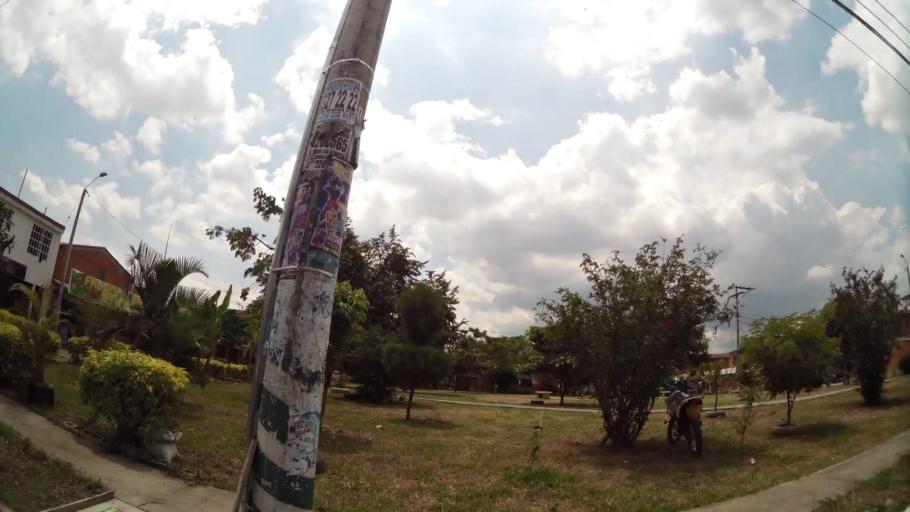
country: CO
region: Valle del Cauca
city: Cali
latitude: 3.4595
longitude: -76.4635
